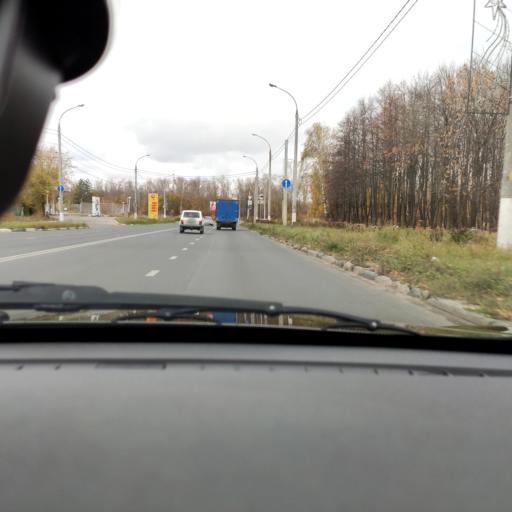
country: RU
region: Samara
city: Tol'yatti
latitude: 53.4974
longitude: 49.2895
